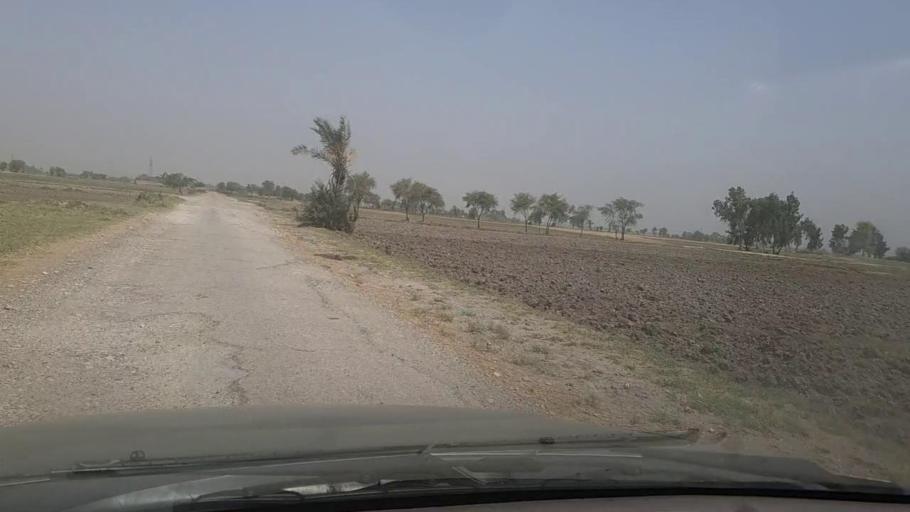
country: PK
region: Sindh
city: Madeji
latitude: 27.8190
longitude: 68.3971
